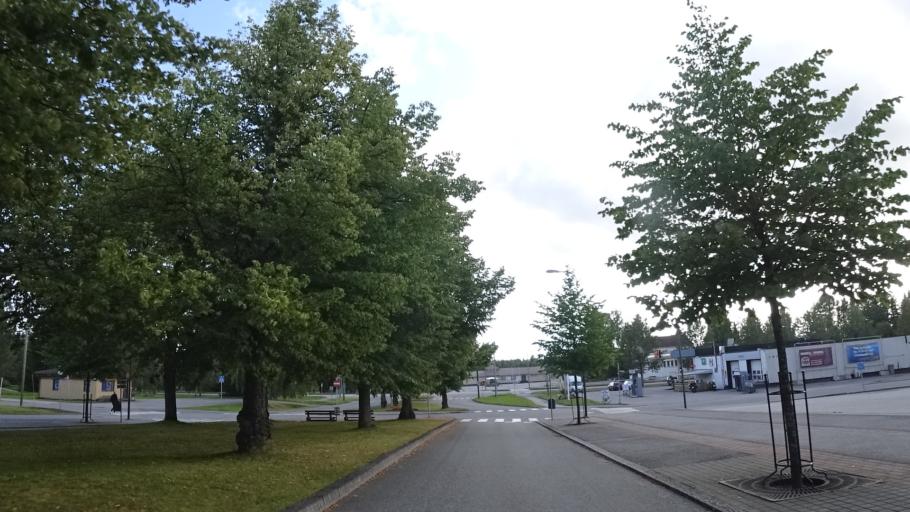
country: FI
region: North Karelia
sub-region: Pielisen Karjala
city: Lieksa
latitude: 63.3195
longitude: 30.0199
